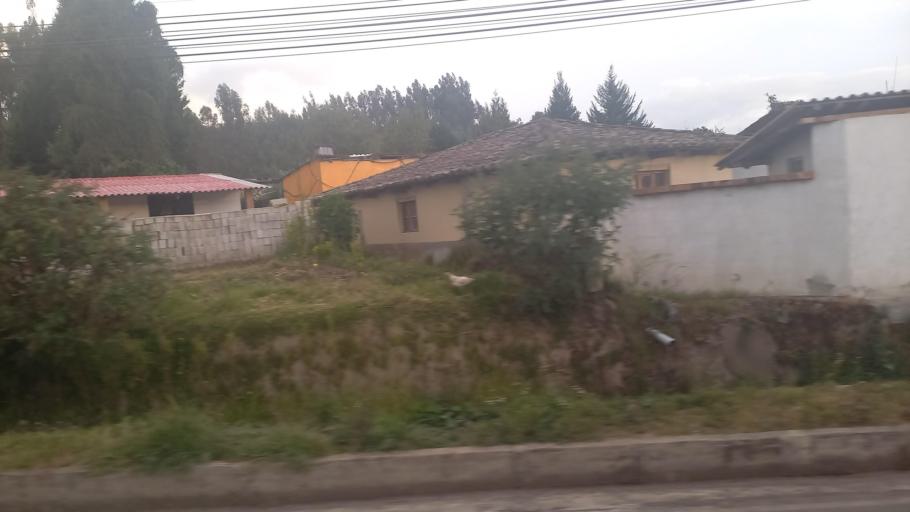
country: EC
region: Pichincha
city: Cayambe
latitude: 0.0839
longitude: -78.1048
